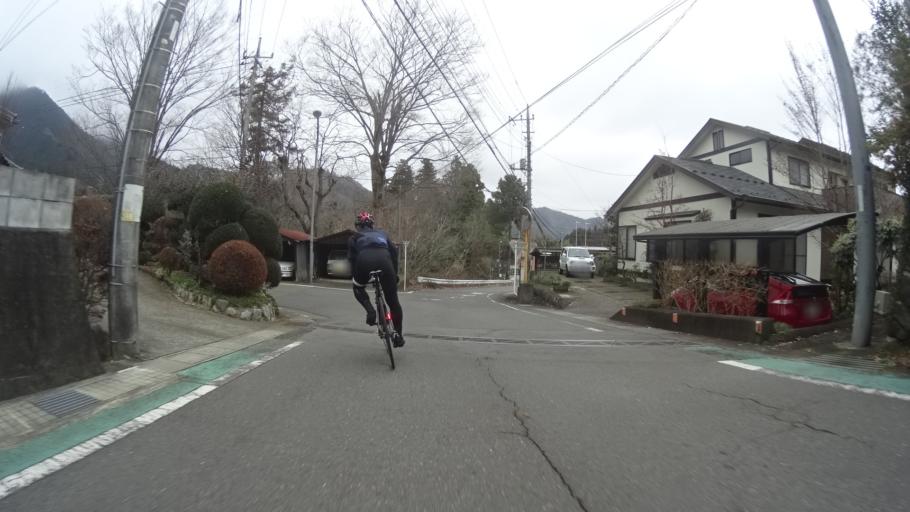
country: JP
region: Yamanashi
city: Uenohara
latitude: 35.6338
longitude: 139.0617
